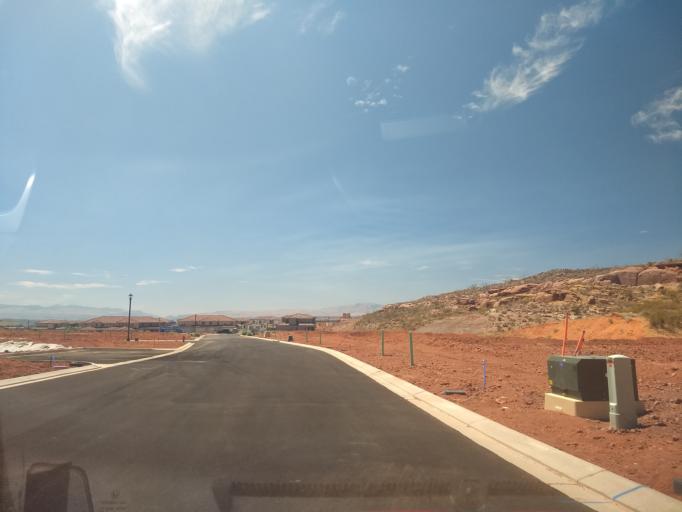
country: US
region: Utah
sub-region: Washington County
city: Washington
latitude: 37.1482
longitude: -113.4697
